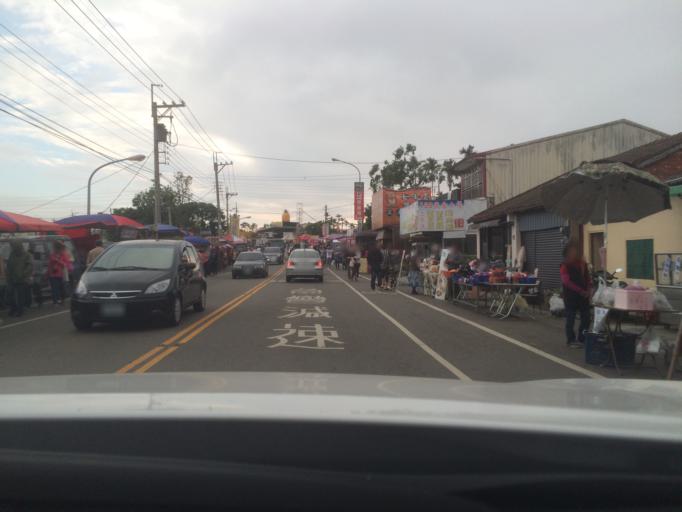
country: TW
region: Taiwan
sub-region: Nantou
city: Nantou
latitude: 23.9345
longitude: 120.6380
